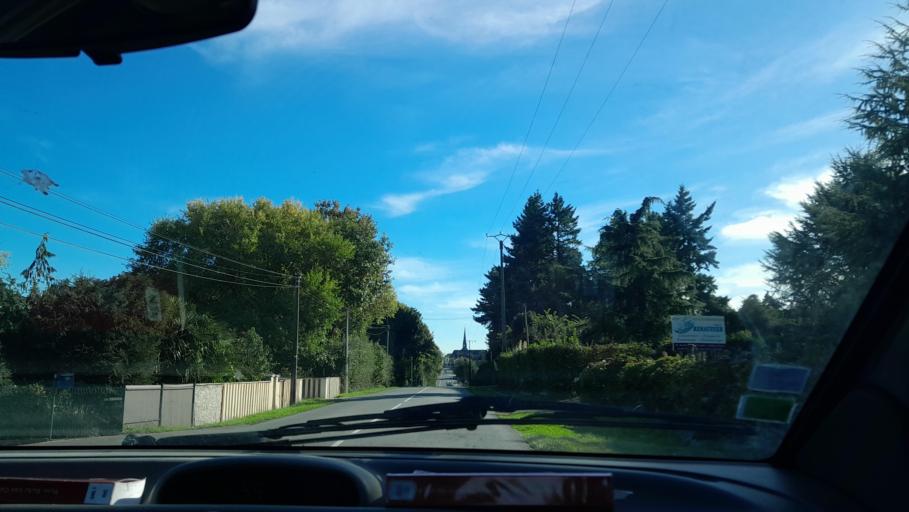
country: FR
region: Brittany
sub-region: Departement d'Ille-et-Vilaine
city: Argentre-du-Plessis
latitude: 47.9763
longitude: -1.1208
